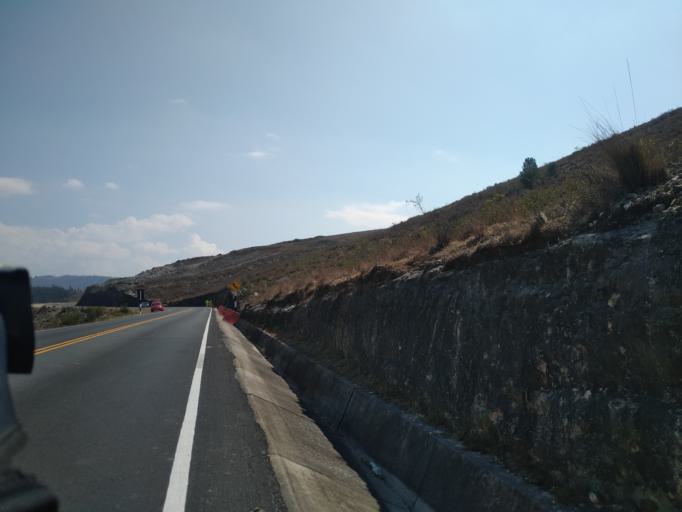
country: PE
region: Cajamarca
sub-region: Provincia de Cajamarca
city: Llacanora
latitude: -7.2102
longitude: -78.3936
